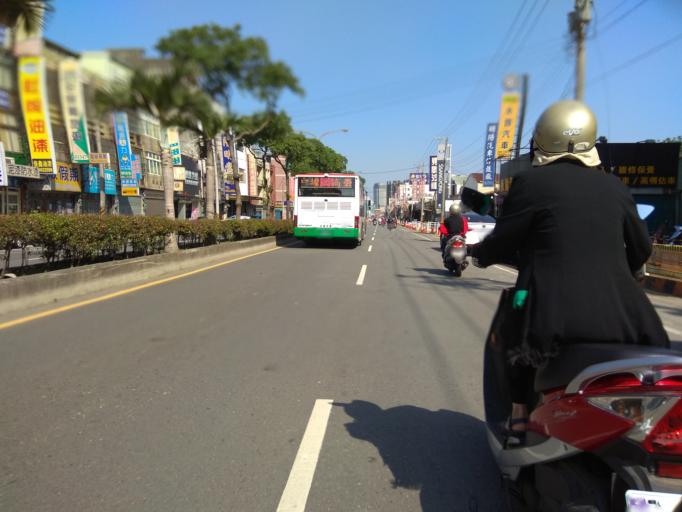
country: TW
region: Taiwan
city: Taoyuan City
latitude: 24.9456
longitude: 121.2091
